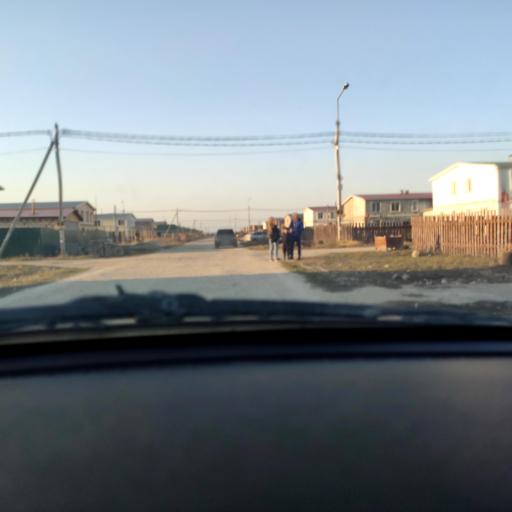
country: RU
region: Samara
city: Podstepki
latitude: 53.5734
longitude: 49.1197
